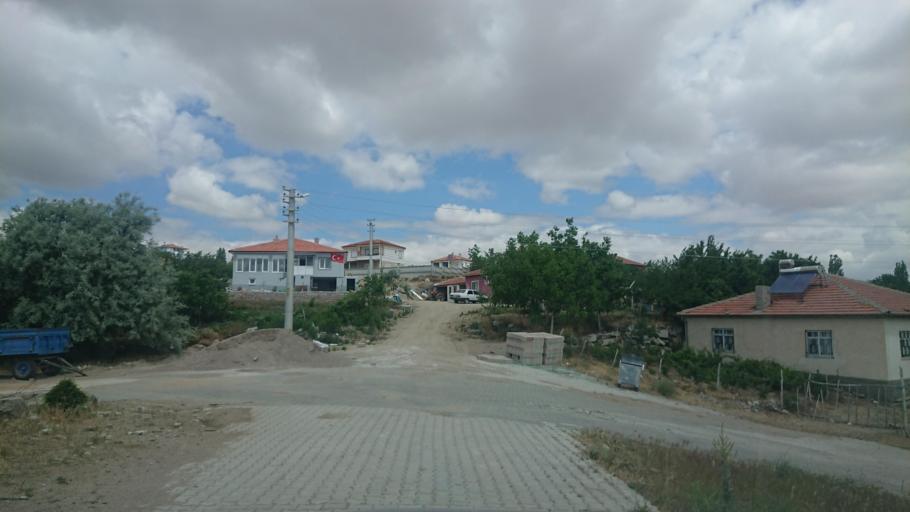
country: TR
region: Aksaray
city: Agacoren
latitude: 38.8667
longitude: 33.9485
